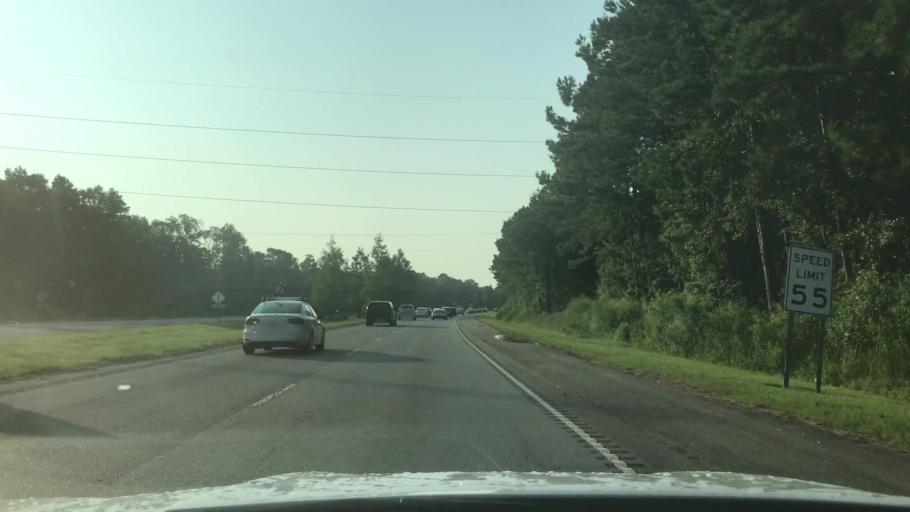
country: US
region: South Carolina
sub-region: Charleston County
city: Shell Point
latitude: 32.8186
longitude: -80.0664
